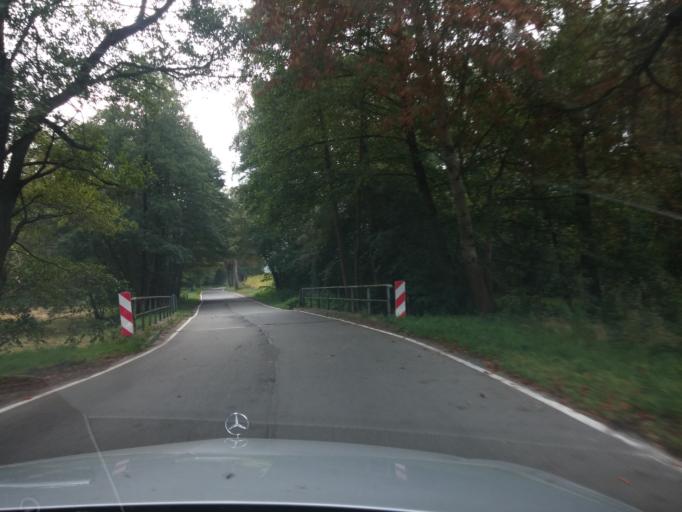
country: DE
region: Brandenburg
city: Putlitz
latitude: 53.2796
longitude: 12.0576
